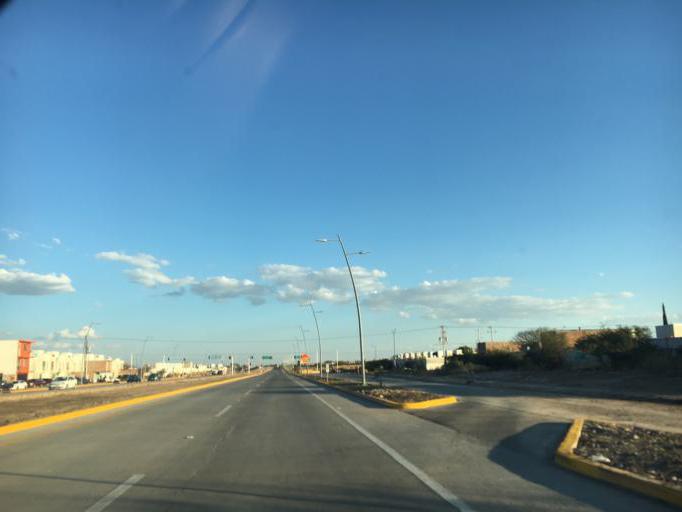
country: MX
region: Guanajuato
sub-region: Leon
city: Fraccionamiento Paraiso Real
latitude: 21.1049
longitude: -101.5790
